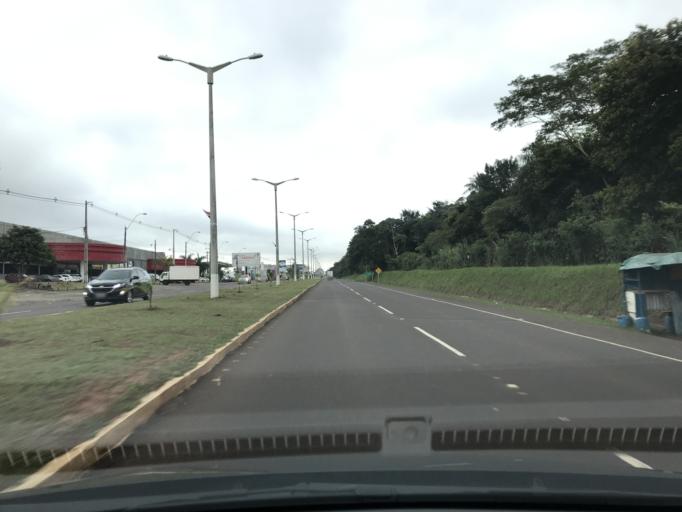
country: PY
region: Canindeyu
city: Salto del Guaira
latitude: -24.0173
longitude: -54.3254
